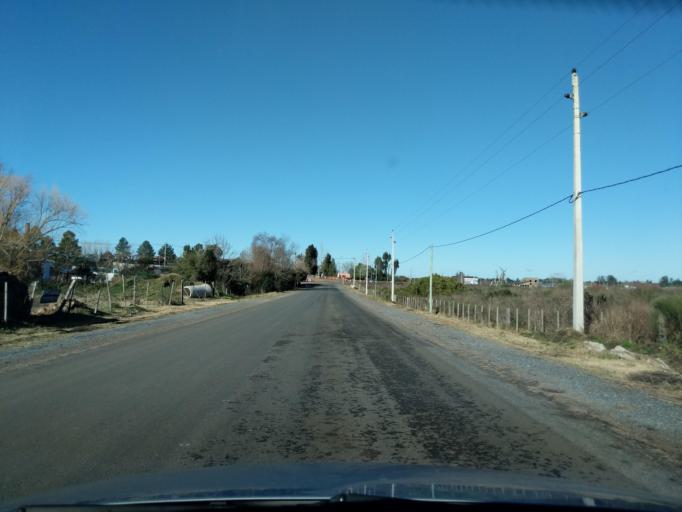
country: UY
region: Florida
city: Florida
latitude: -34.1022
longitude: -56.2422
